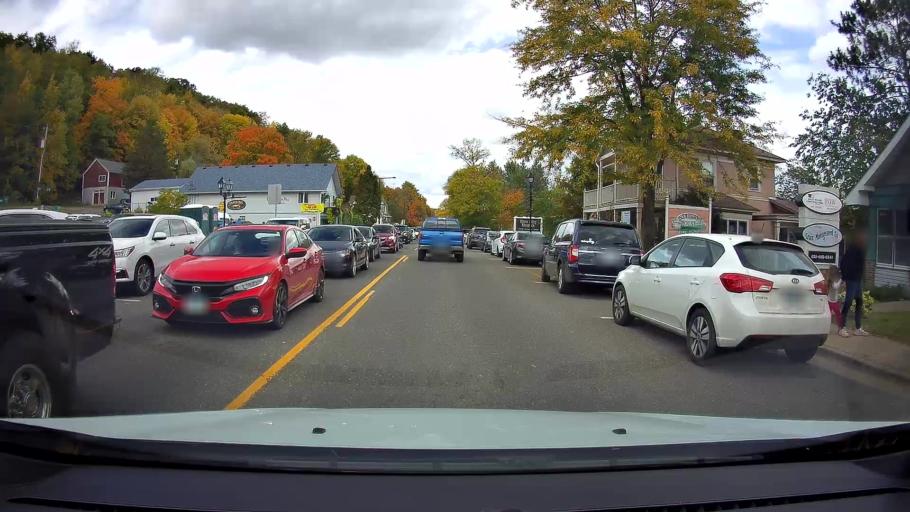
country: US
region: Wisconsin
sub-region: Polk County
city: Saint Croix Falls
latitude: 45.4027
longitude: -92.6526
